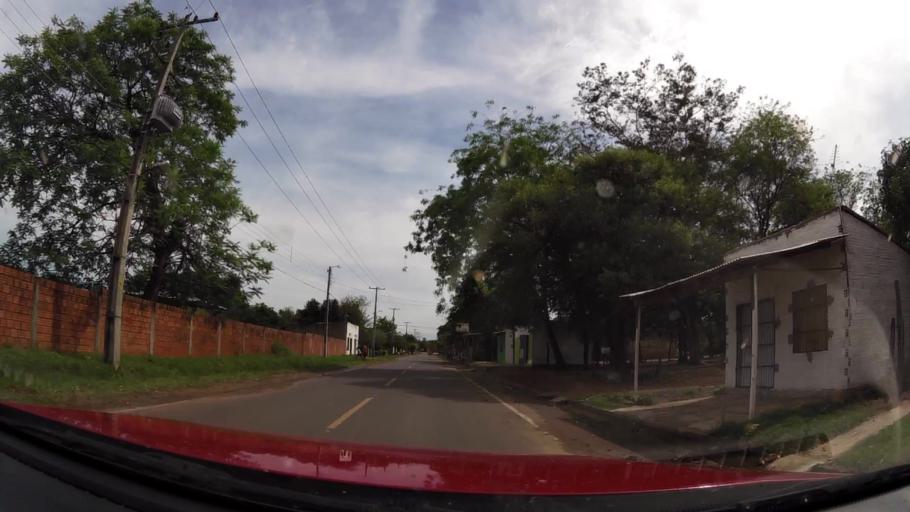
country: PY
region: Central
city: Limpio
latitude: -25.1769
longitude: -57.4739
